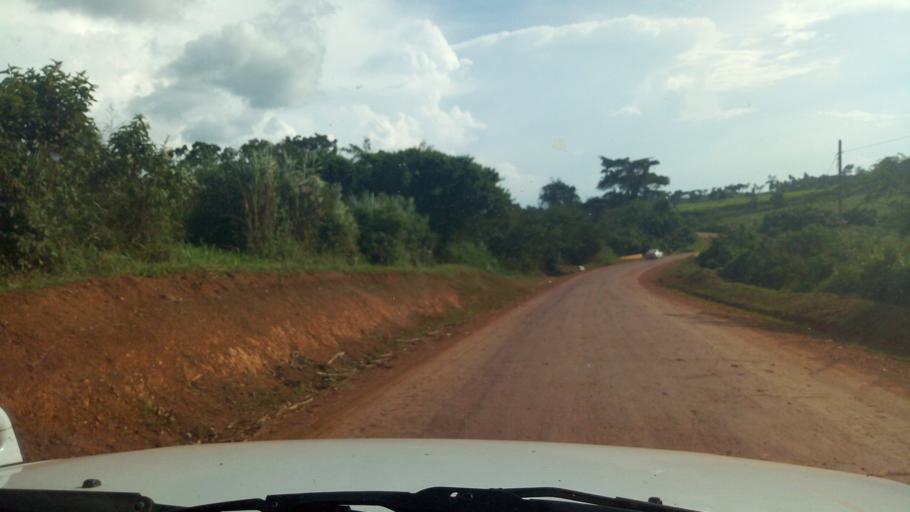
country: UG
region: Western Region
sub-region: Masindi District
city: Masindi
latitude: 1.6702
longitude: 31.6523
